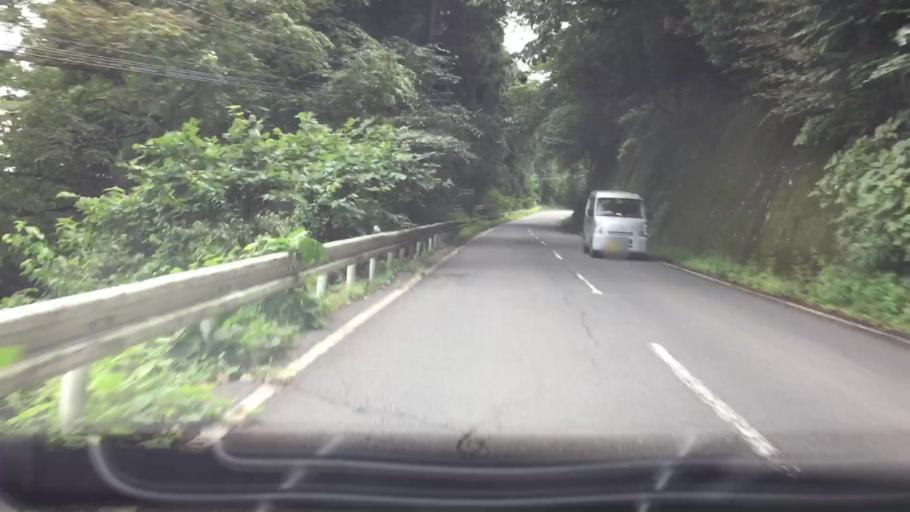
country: JP
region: Tochigi
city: Imaichi
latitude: 36.7617
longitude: 139.6804
